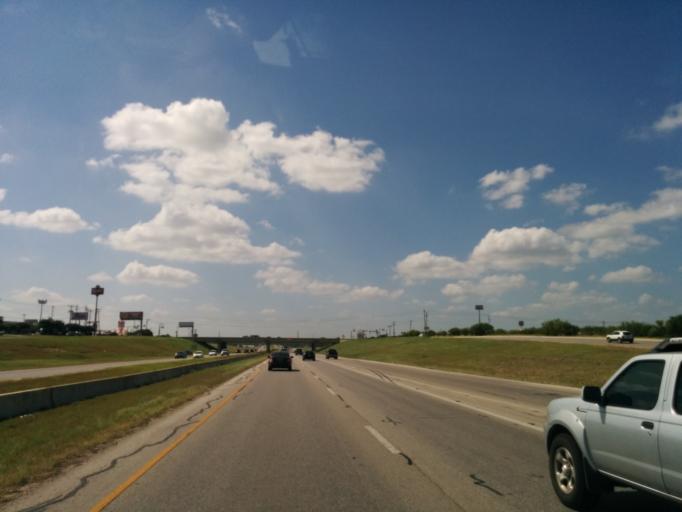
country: US
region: Texas
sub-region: Bexar County
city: Live Oak
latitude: 29.5893
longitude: -98.3501
